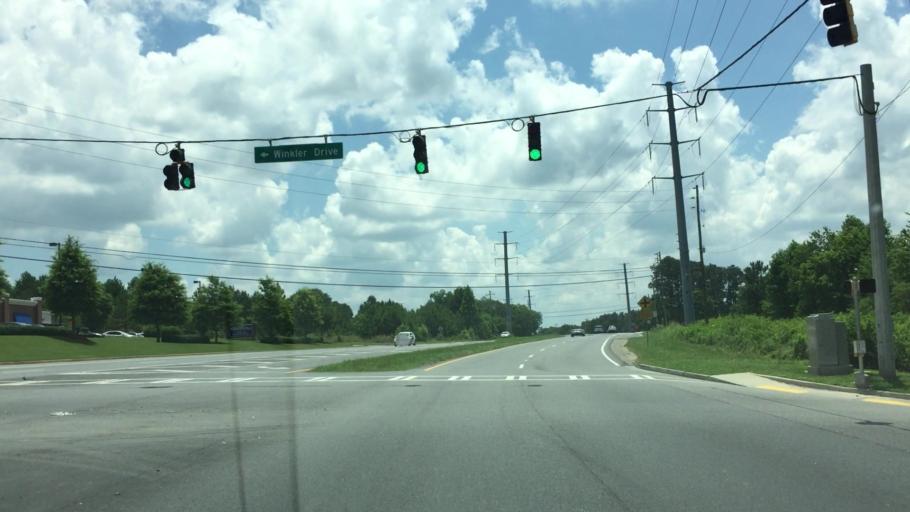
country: US
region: Georgia
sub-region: Fulton County
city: Milton
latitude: 34.1343
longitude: -84.2400
